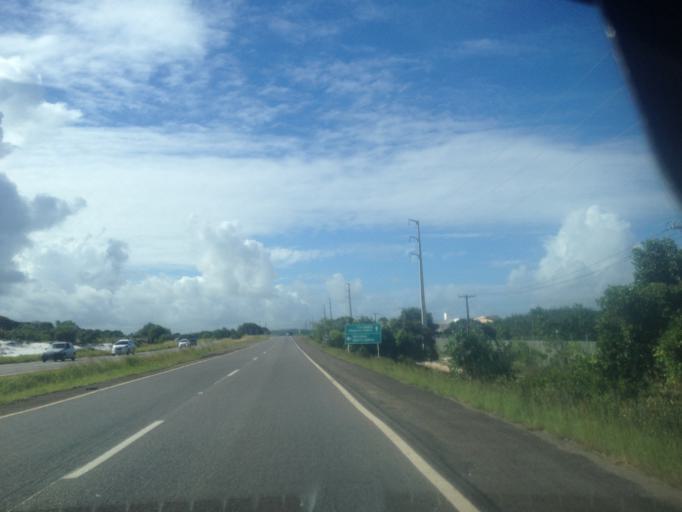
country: BR
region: Bahia
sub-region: Mata De Sao Joao
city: Mata de Sao Joao
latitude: -12.6206
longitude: -38.0584
